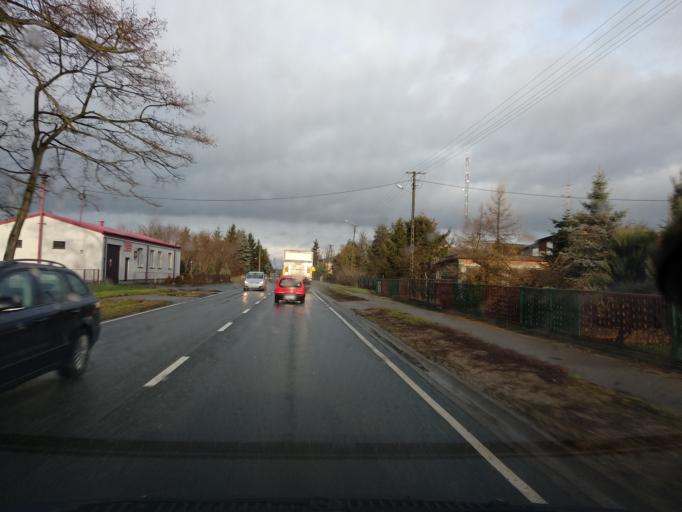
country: PL
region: Greater Poland Voivodeship
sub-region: Powiat koninski
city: Rychwal
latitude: 52.1199
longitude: 18.1692
